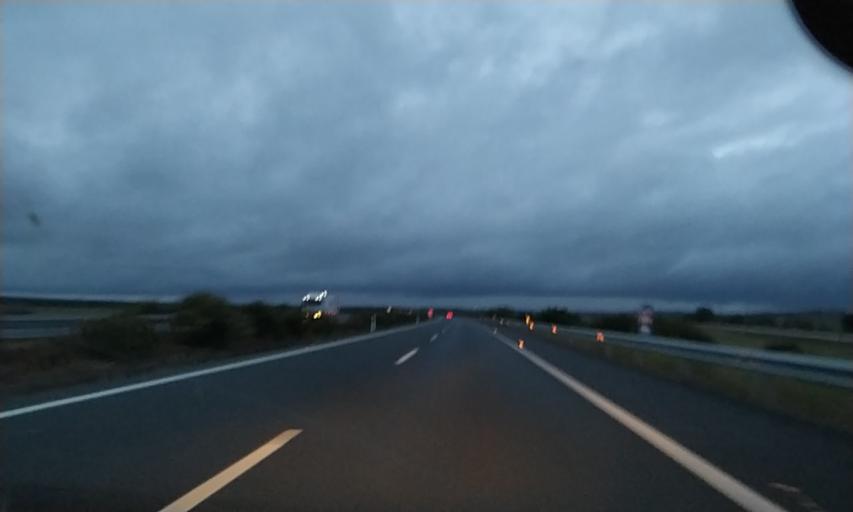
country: ES
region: Extremadura
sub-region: Provincia de Caceres
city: Casas de Don Antonio
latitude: 39.2527
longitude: -6.3091
